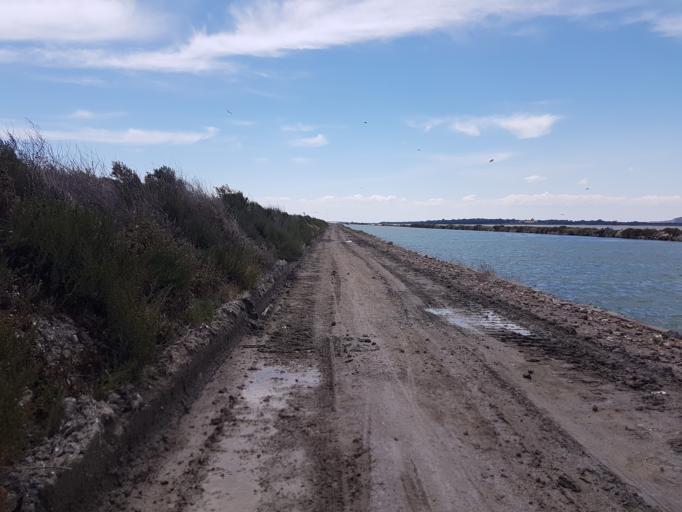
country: FR
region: Languedoc-Roussillon
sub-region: Departement de l'Herault
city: Vic-la-Gardiole
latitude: 43.4817
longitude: 3.8365
